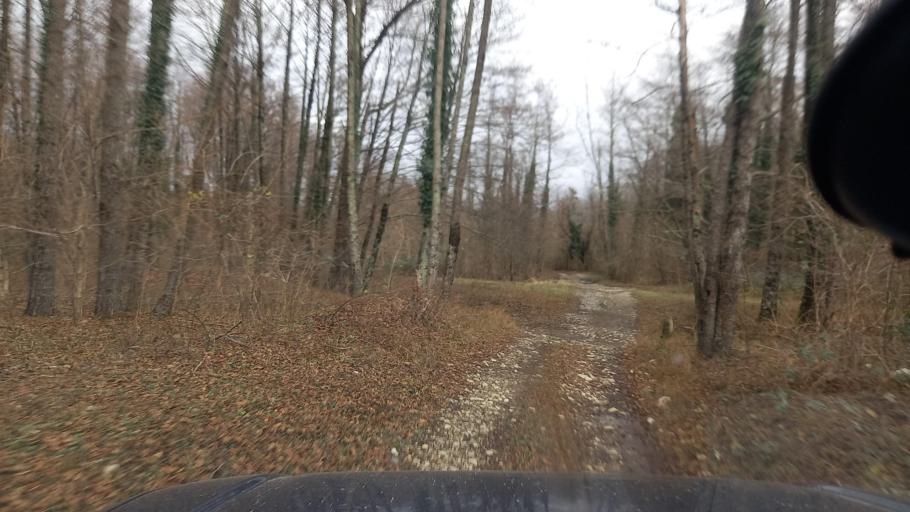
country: RU
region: Krasnodarskiy
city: Pshada
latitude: 44.4875
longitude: 38.4130
